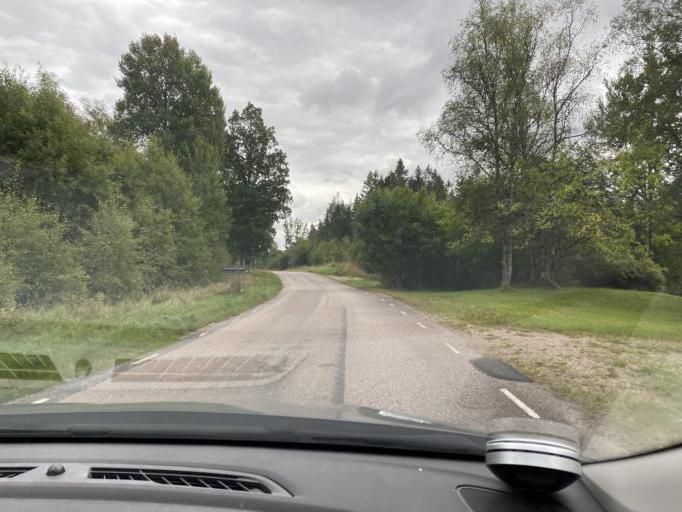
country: SE
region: Kronoberg
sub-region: Markaryds Kommun
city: Markaryd
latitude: 56.4865
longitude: 13.5570
